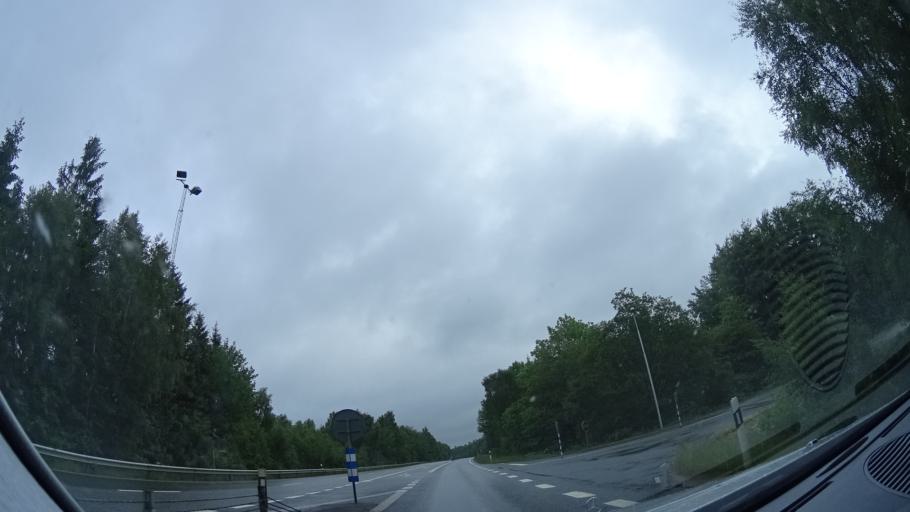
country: SE
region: Skane
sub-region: Hoors Kommun
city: Satofta
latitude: 55.9164
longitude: 13.5310
